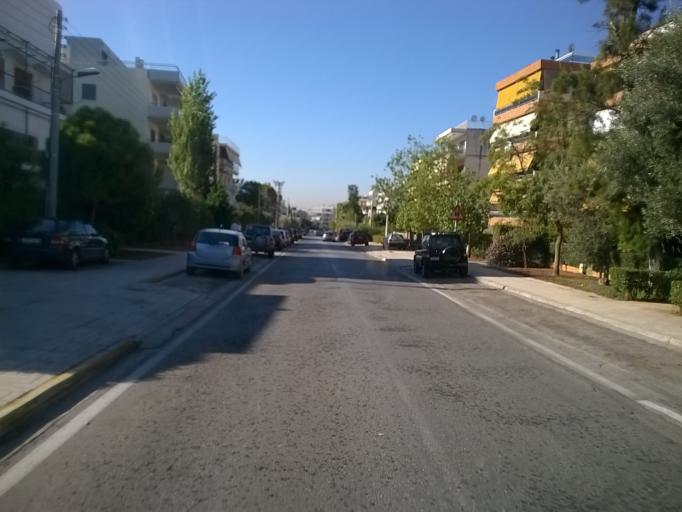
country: GR
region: Attica
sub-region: Nomarchia Athinas
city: Glyfada
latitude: 37.8687
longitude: 23.7534
